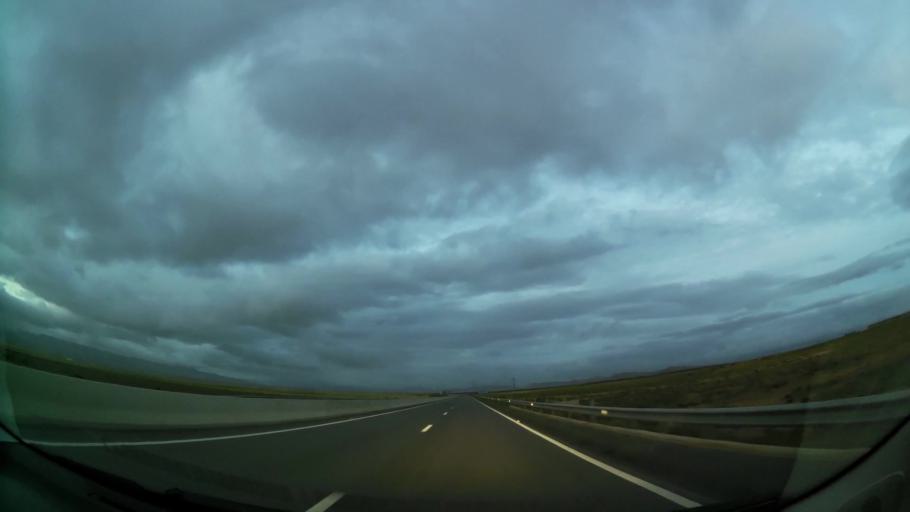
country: MA
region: Oriental
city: El Aioun
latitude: 34.6312
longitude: -2.3408
